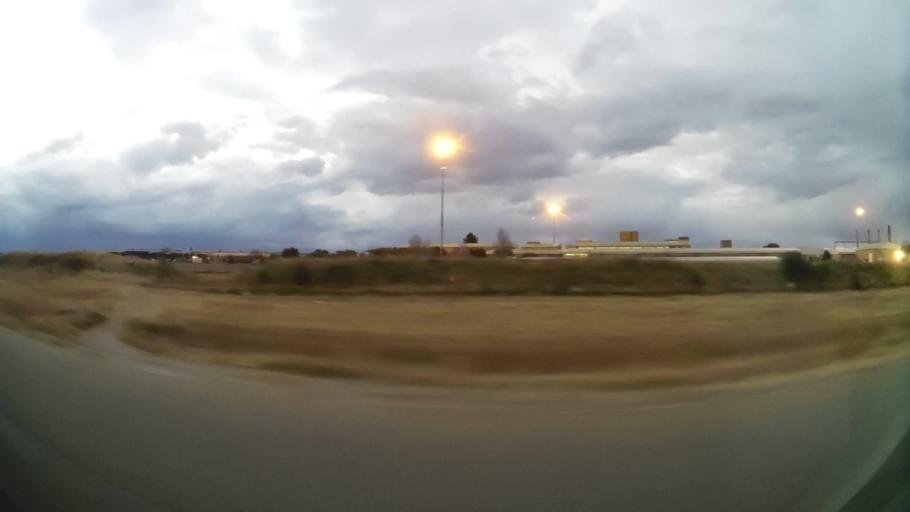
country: ZA
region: Orange Free State
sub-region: Lejweleputswa District Municipality
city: Welkom
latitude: -27.9540
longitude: 26.7876
